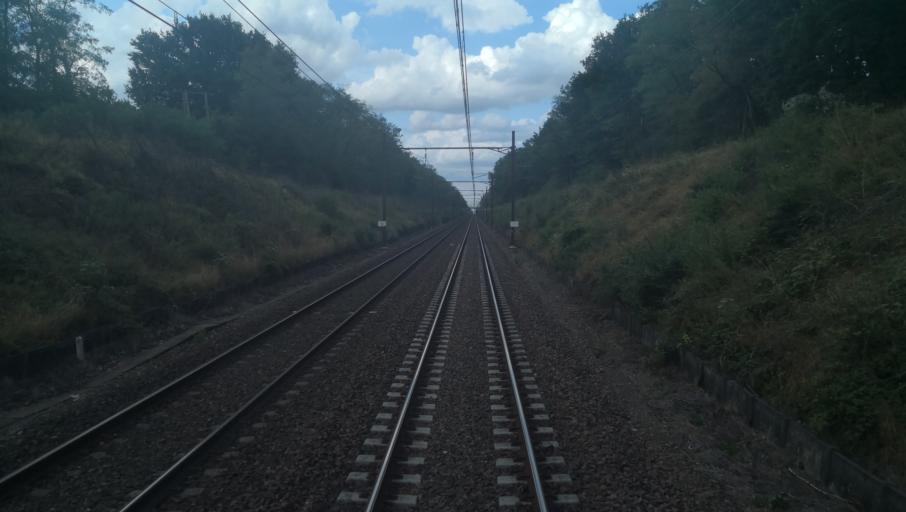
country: FR
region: Centre
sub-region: Departement du Loiret
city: La Ferte-Saint-Aubin
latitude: 47.7450
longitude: 1.9328
